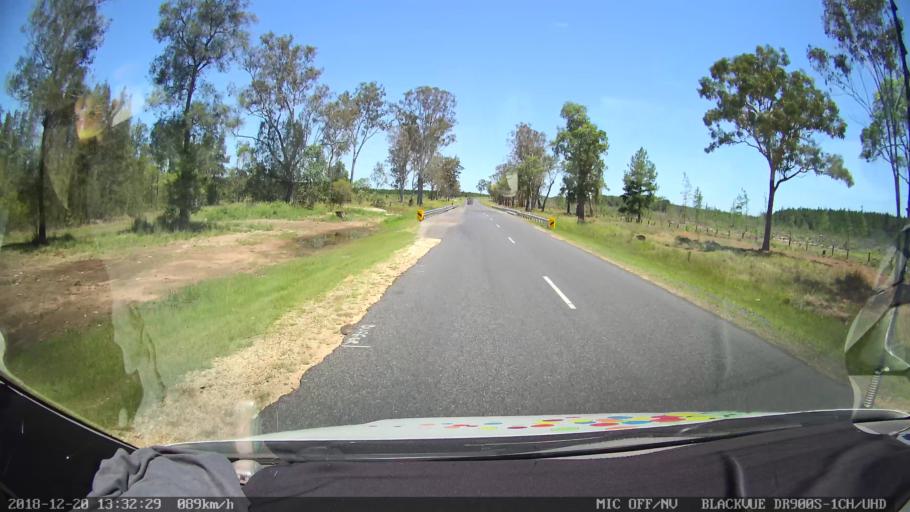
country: AU
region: New South Wales
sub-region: Clarence Valley
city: Gordon
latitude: -29.2324
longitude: 152.9890
